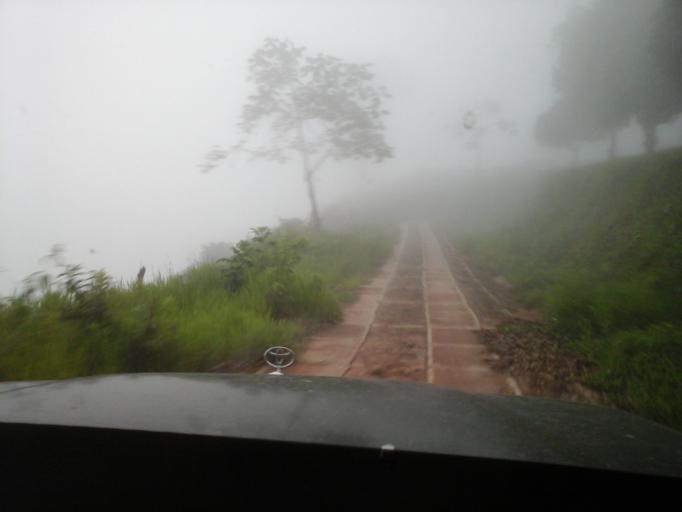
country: CO
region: Cesar
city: Agustin Codazzi
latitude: 9.9421
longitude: -73.1278
